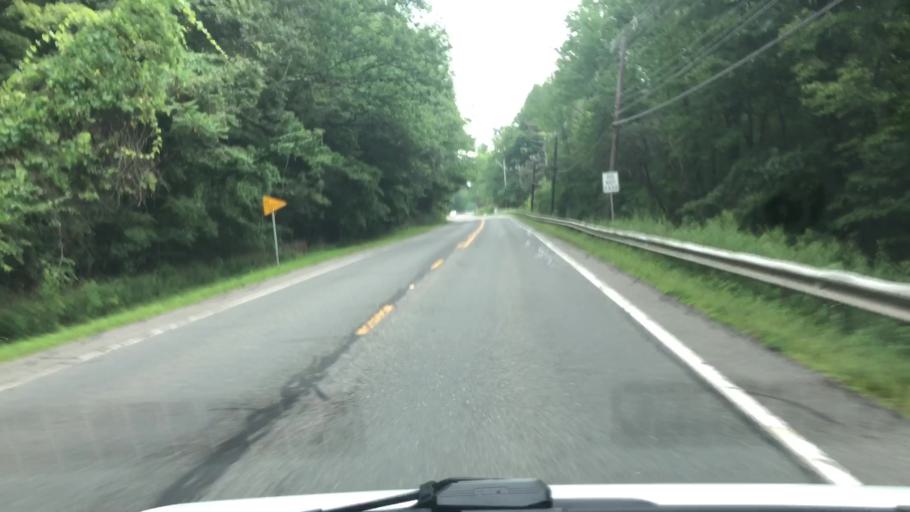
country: US
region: Massachusetts
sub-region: Berkshire County
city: Williamstown
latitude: 42.6890
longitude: -73.2295
